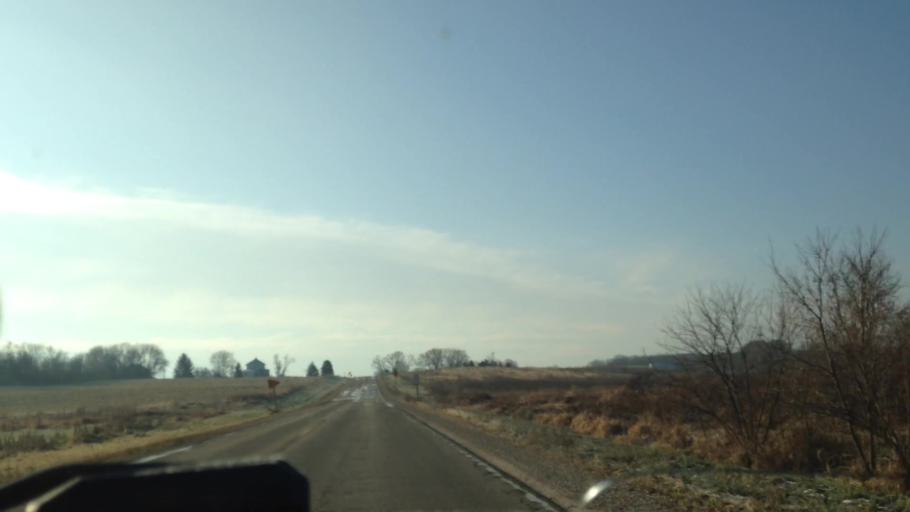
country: US
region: Wisconsin
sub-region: Dodge County
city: Mayville
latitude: 43.4471
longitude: -88.5001
